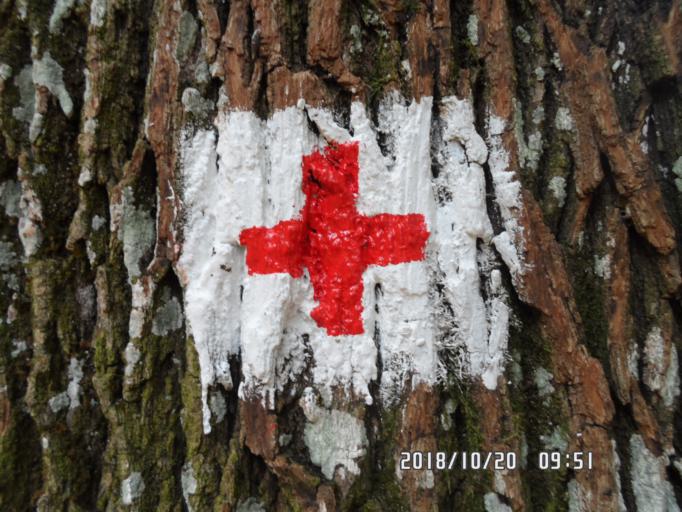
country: HU
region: Veszprem
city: Herend
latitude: 47.2030
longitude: 17.7217
